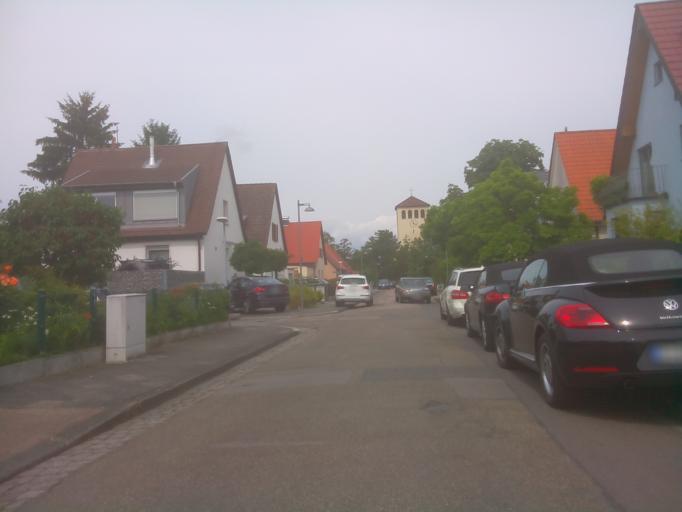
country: DE
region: Baden-Wuerttemberg
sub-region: Karlsruhe Region
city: Mannheim
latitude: 49.5294
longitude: 8.4992
